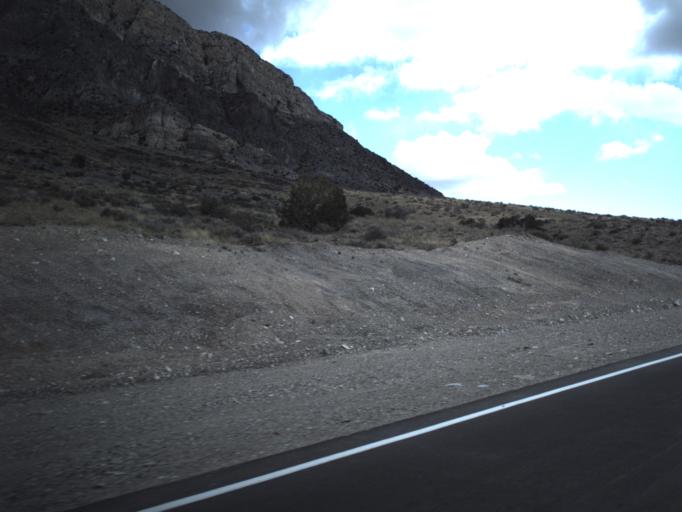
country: US
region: Utah
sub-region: Beaver County
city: Milford
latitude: 38.5058
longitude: -113.6000
